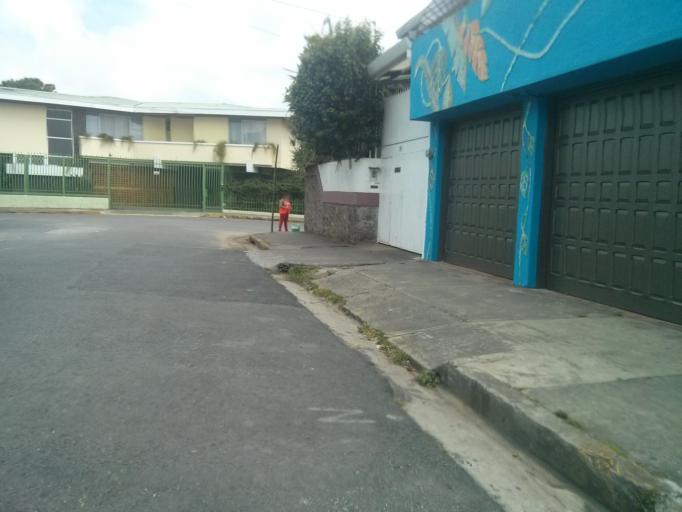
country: CR
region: San Jose
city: San Pedro
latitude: 9.9348
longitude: -84.0616
